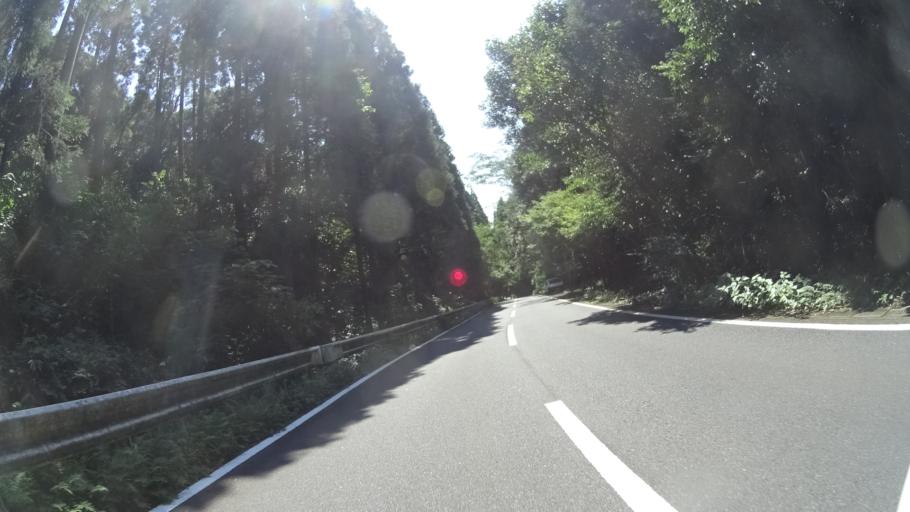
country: JP
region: Kagoshima
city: Kajiki
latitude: 31.7550
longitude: 130.6701
